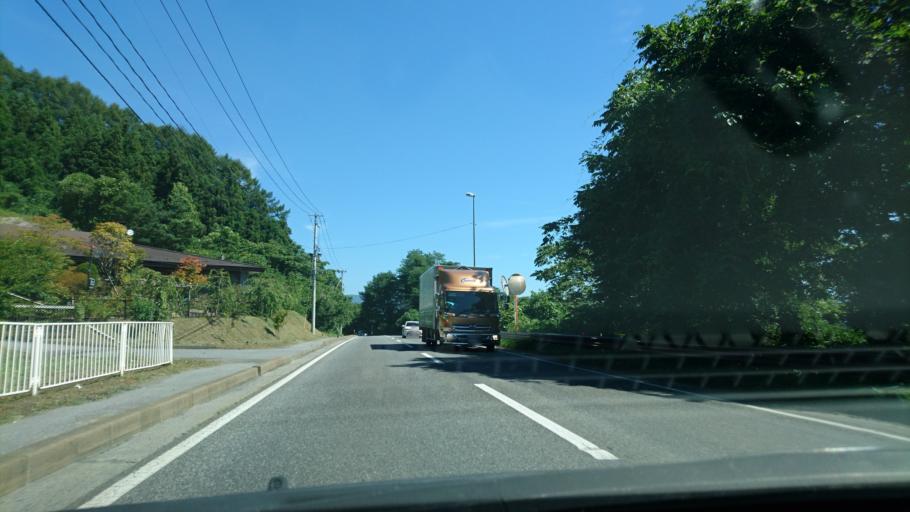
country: JP
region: Iwate
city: Tono
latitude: 39.3335
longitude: 141.5186
